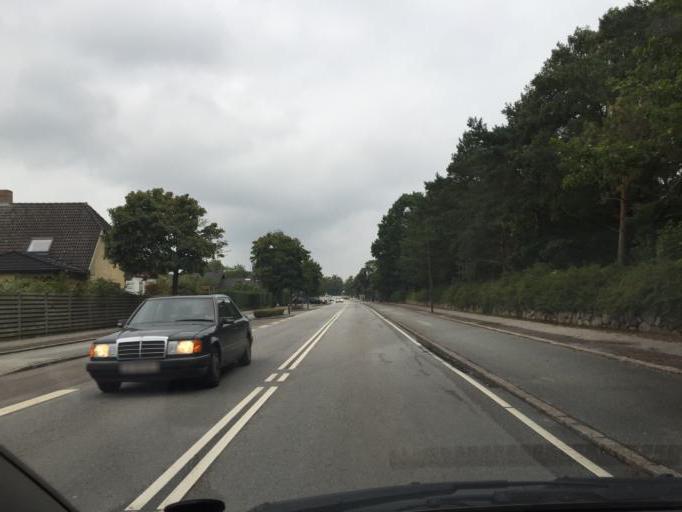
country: DK
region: Capital Region
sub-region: Herlev Kommune
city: Herlev
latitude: 55.7327
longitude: 12.4352
